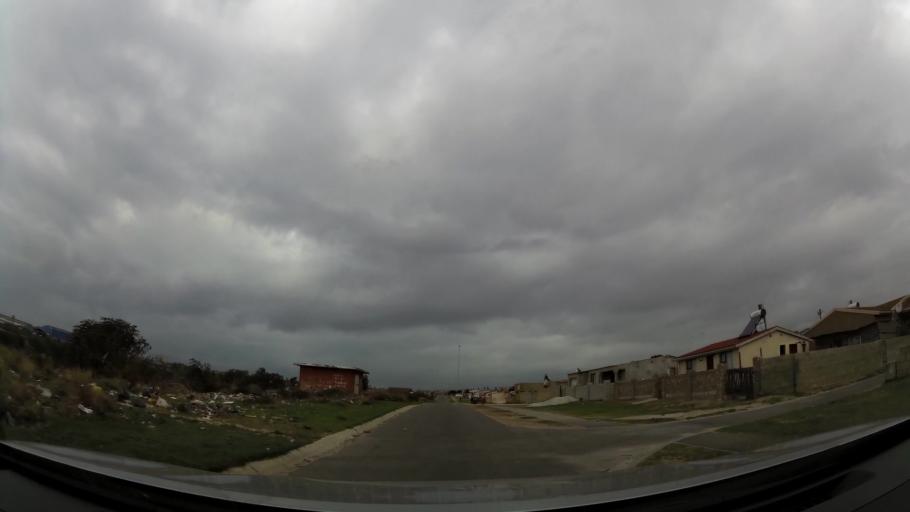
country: ZA
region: Eastern Cape
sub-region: Nelson Mandela Bay Metropolitan Municipality
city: Port Elizabeth
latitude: -33.8777
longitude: 25.6008
